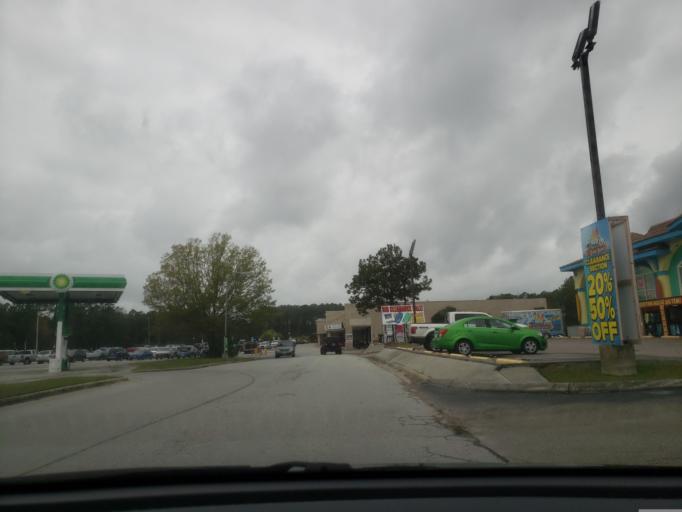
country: US
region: North Carolina
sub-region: Onslow County
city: Sneads Ferry
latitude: 34.5269
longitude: -77.4354
